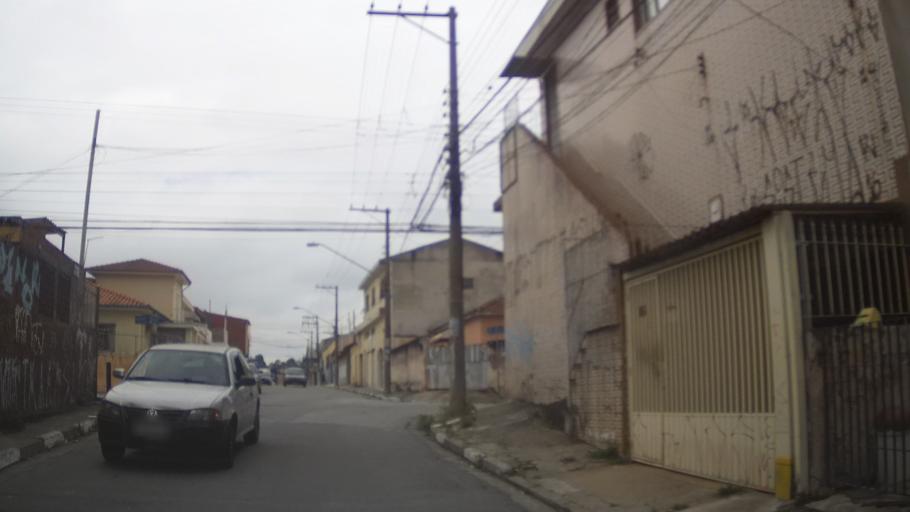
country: BR
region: Sao Paulo
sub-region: Guarulhos
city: Guarulhos
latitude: -23.4673
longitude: -46.5550
